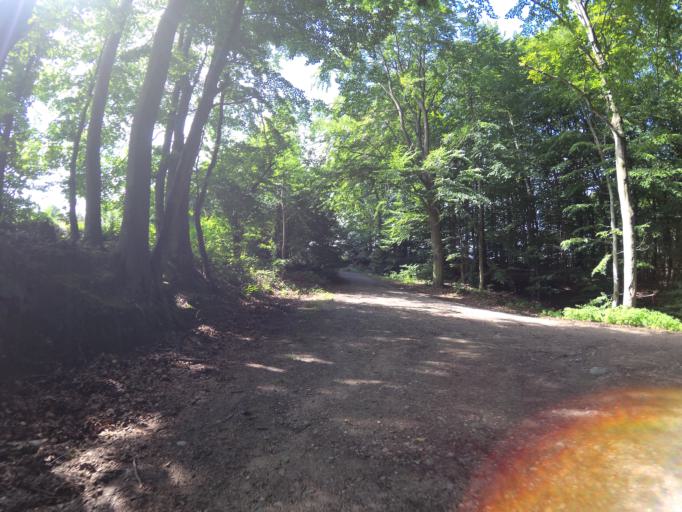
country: PL
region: Pomeranian Voivodeship
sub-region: Powiat wejherowski
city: Bojano
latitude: 54.5016
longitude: 18.4348
